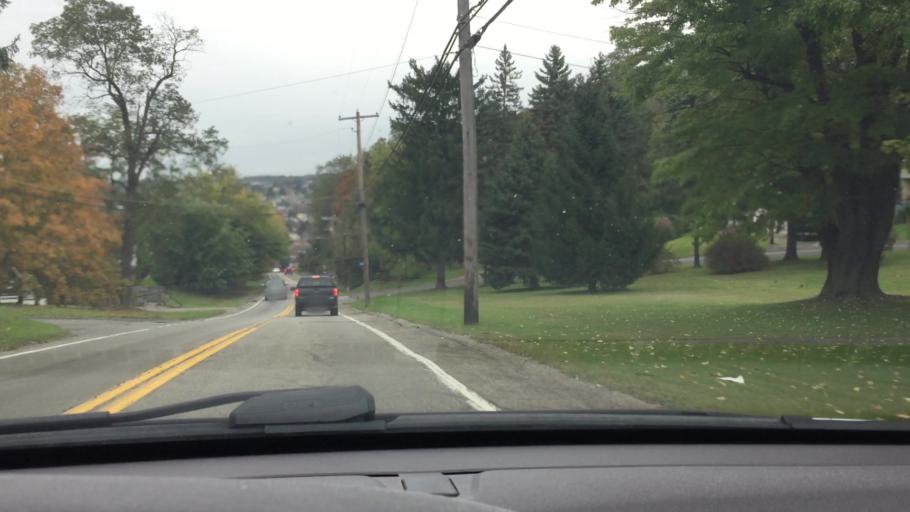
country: US
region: Pennsylvania
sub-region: Washington County
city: Canonsburg
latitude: 40.2553
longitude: -80.1730
